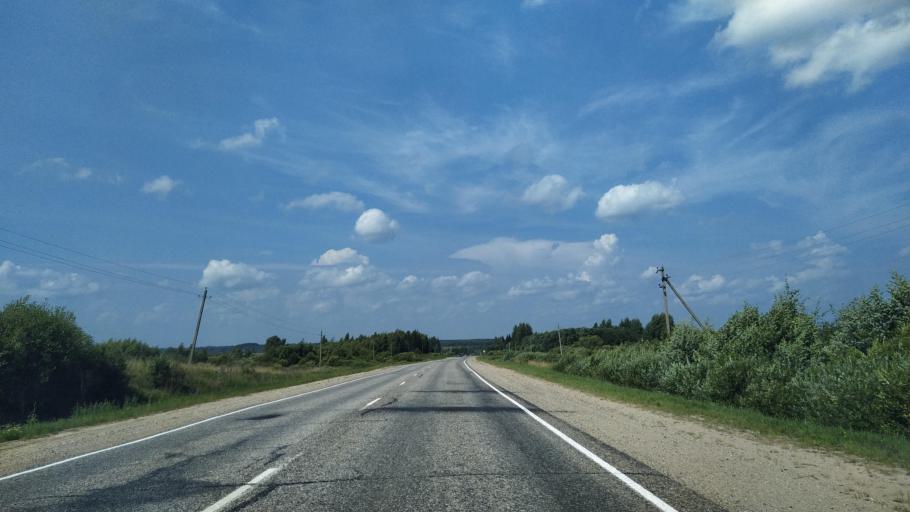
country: RU
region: Pskov
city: Pushkinskiye Gory
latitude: 57.0160
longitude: 28.8861
